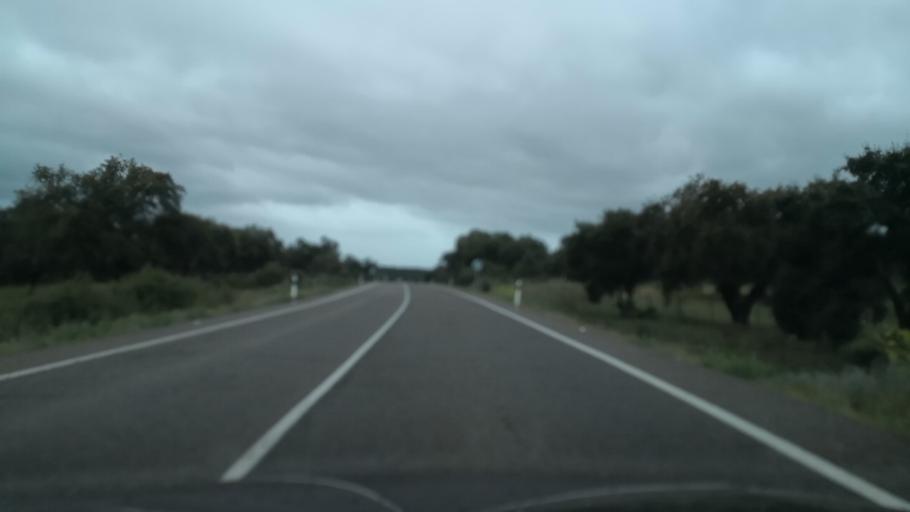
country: ES
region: Extremadura
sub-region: Provincia de Badajoz
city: Puebla de Obando
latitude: 39.1478
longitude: -6.6520
